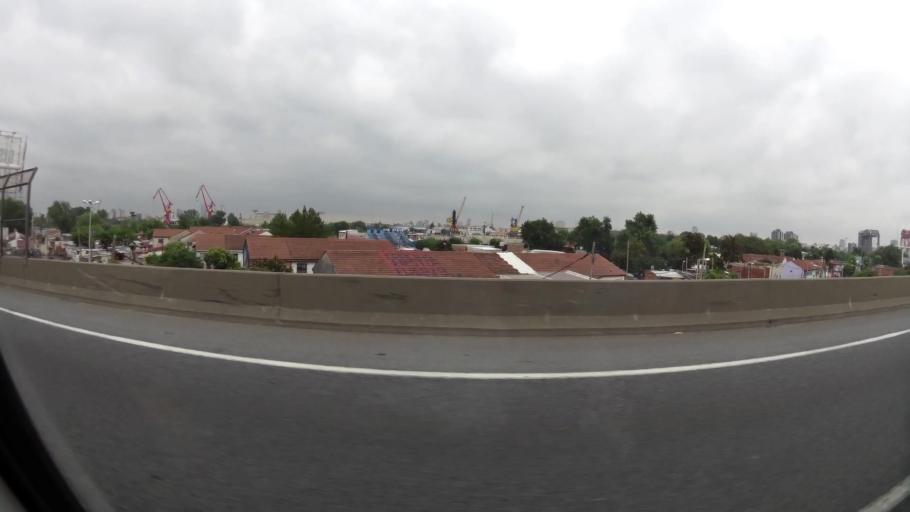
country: AR
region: Buenos Aires
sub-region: Partido de Avellaneda
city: Avellaneda
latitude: -34.6436
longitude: -58.3505
